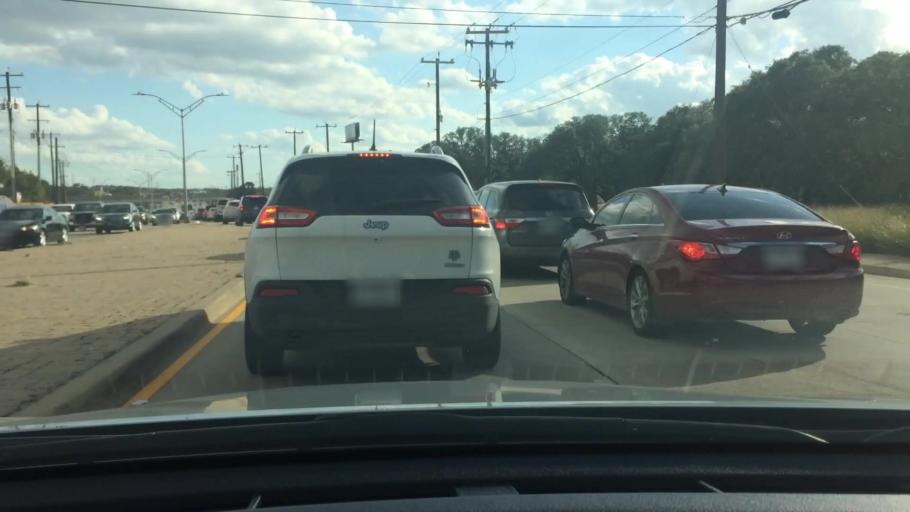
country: US
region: Texas
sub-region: Bexar County
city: Hollywood Park
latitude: 29.6038
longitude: -98.4188
